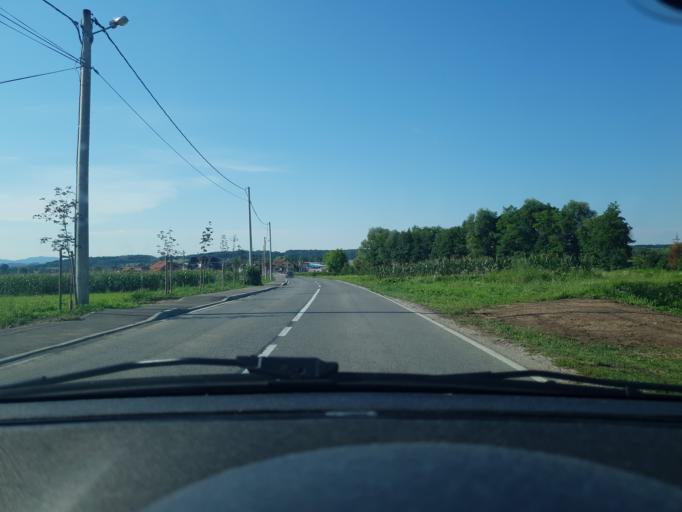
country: HR
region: Zagrebacka
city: Jablanovec
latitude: 45.8952
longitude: 15.8581
